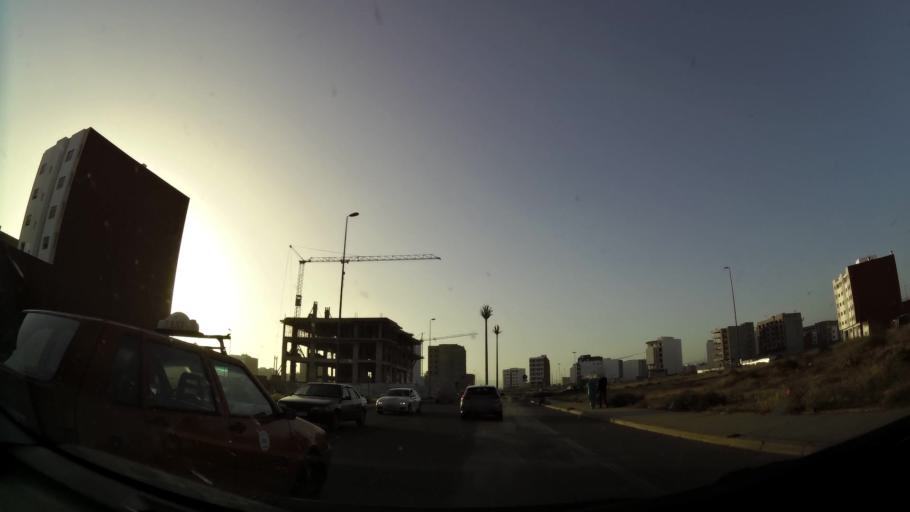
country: MA
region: Oued ed Dahab-Lagouira
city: Dakhla
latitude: 30.3982
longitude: -9.5768
